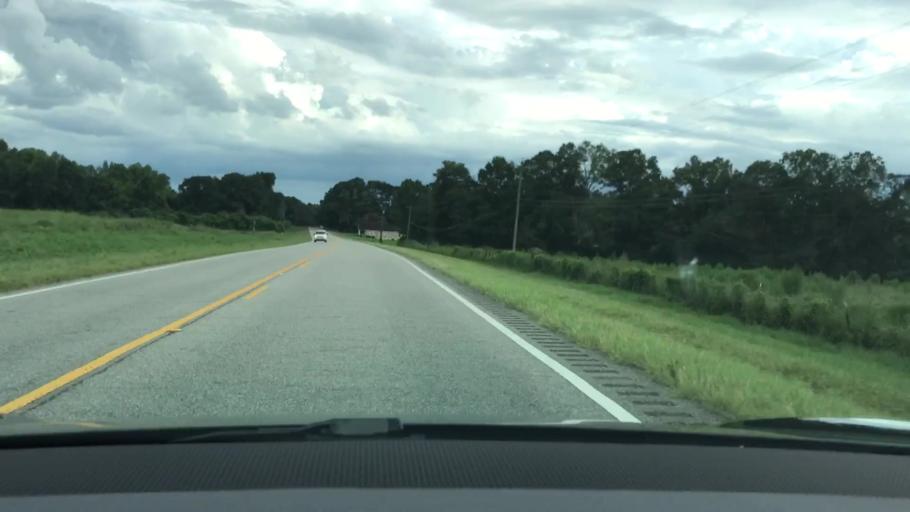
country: US
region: Alabama
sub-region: Coffee County
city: Elba
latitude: 31.5857
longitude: -86.0005
